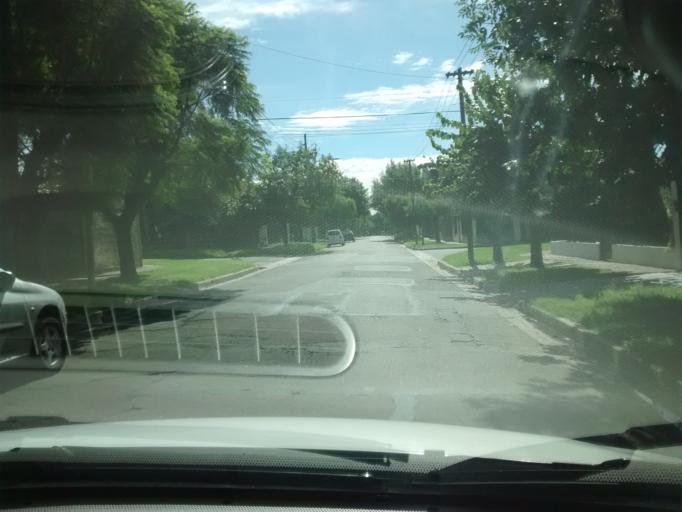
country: AR
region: Buenos Aires
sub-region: Partido de Moron
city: Moron
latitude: -34.6676
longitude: -58.6122
